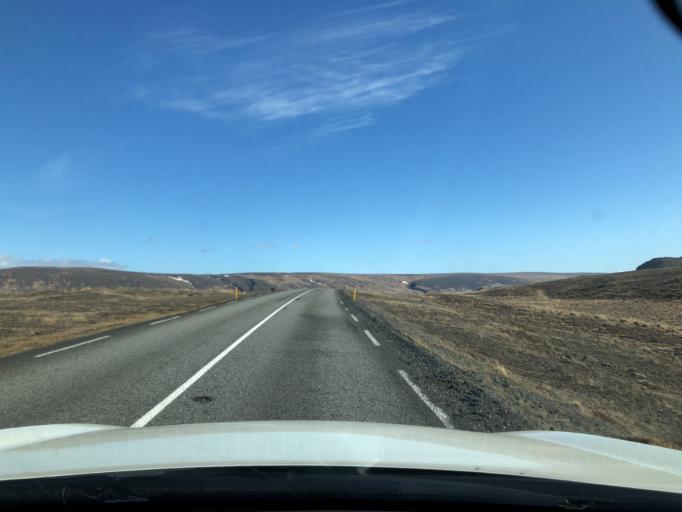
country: IS
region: Capital Region
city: Mosfellsbaer
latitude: 64.6735
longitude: -21.2587
